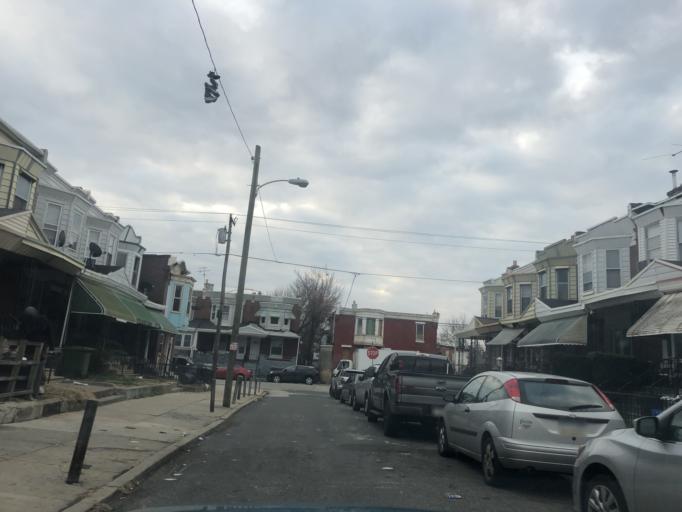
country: US
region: Pennsylvania
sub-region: Delaware County
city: Millbourne
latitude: 39.9758
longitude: -75.2342
